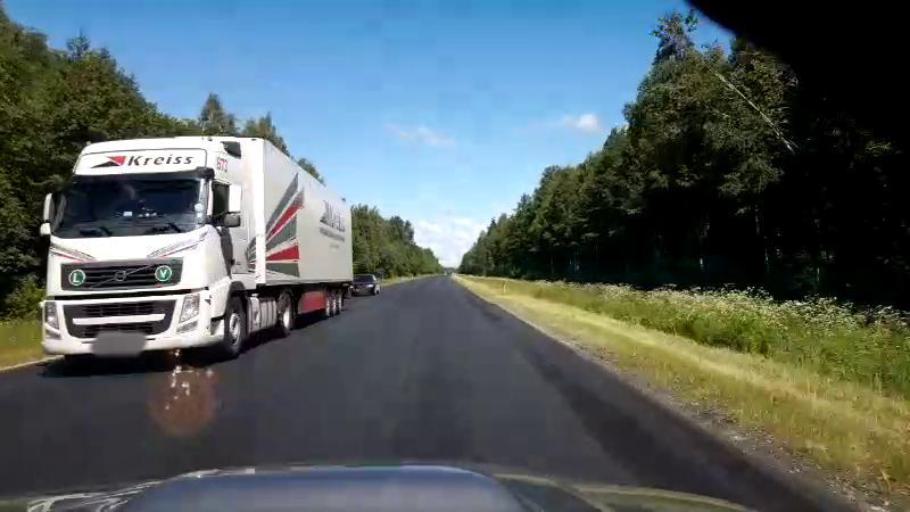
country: LV
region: Salacgrivas
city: Ainazi
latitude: 57.9501
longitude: 24.4367
